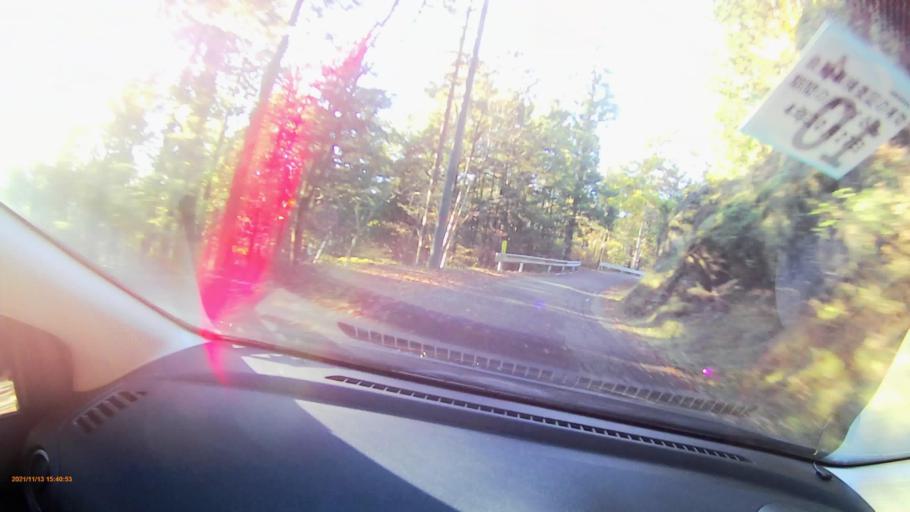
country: JP
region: Gifu
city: Nakatsugawa
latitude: 35.5855
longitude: 137.3888
